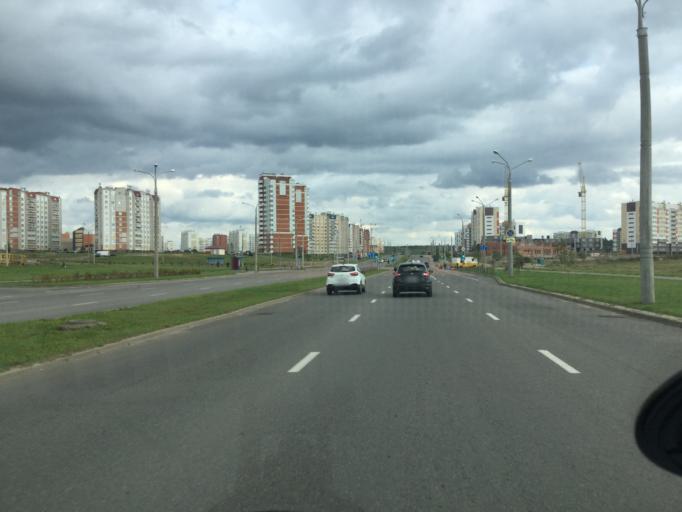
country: BY
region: Vitebsk
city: Vitebsk
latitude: 55.1654
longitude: 30.2621
